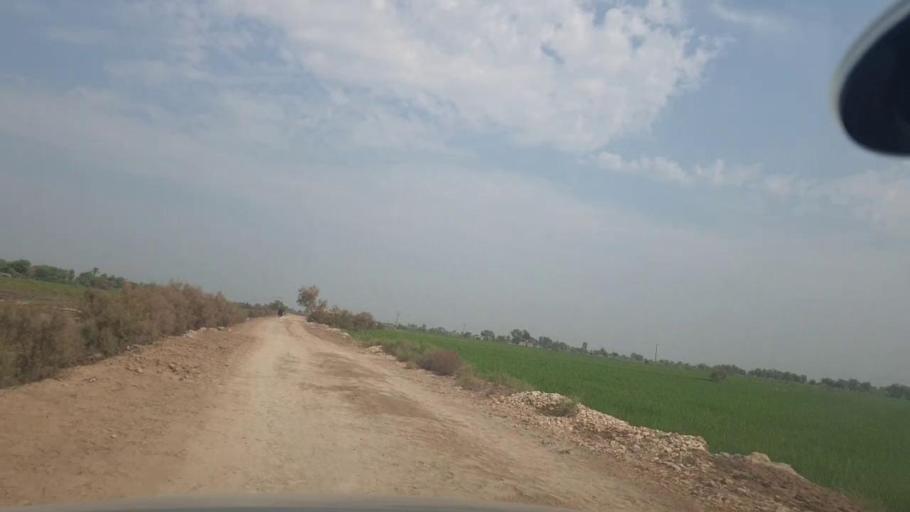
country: PK
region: Balochistan
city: Mehrabpur
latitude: 28.1031
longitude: 68.0921
